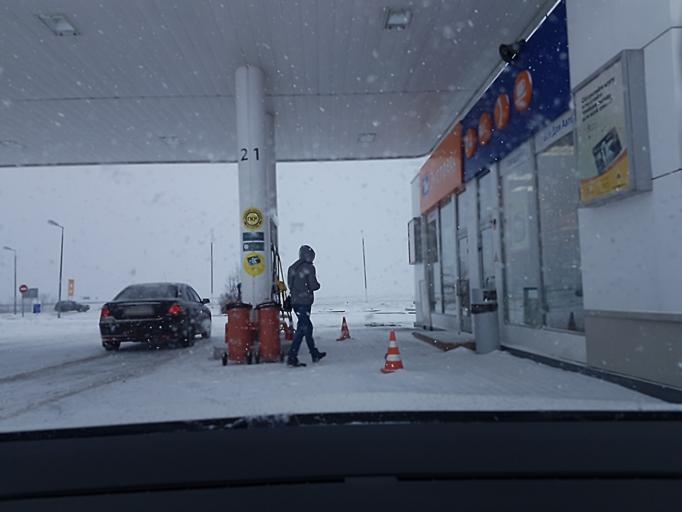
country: RU
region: Rjazan
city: Ryazhsk
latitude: 53.6566
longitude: 39.9833
